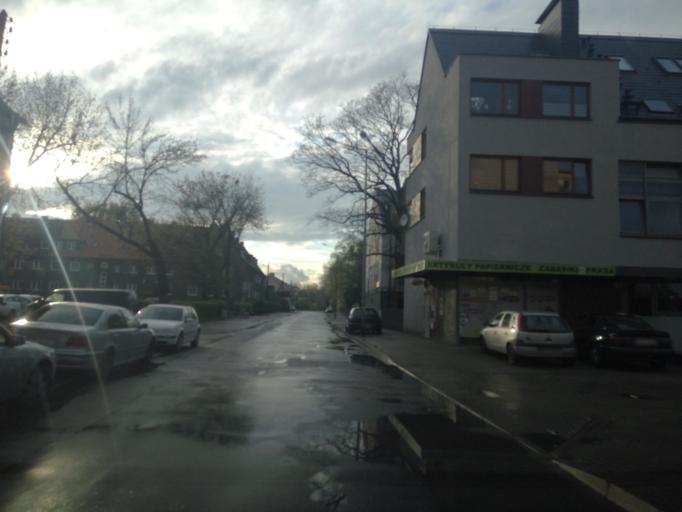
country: PL
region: Lower Silesian Voivodeship
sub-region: Powiat wroclawski
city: Radwanice
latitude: 51.0607
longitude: 17.0824
